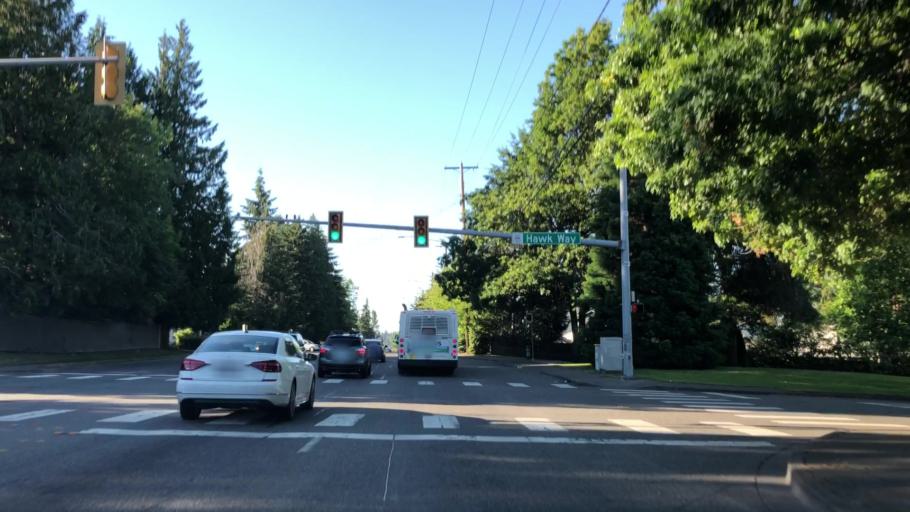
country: US
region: Washington
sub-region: Snohomish County
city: Mountlake Terrace
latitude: 47.8017
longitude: -122.2922
